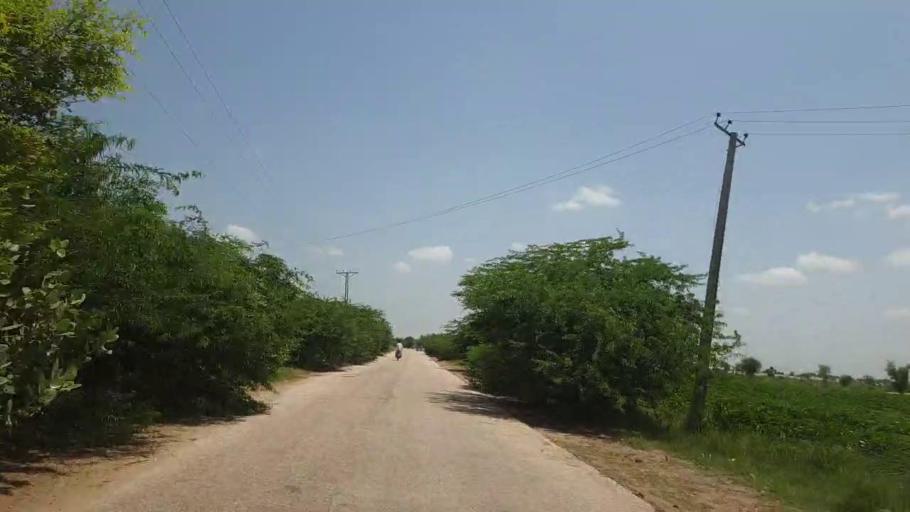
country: PK
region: Sindh
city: Pano Aqil
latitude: 27.6677
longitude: 69.2288
